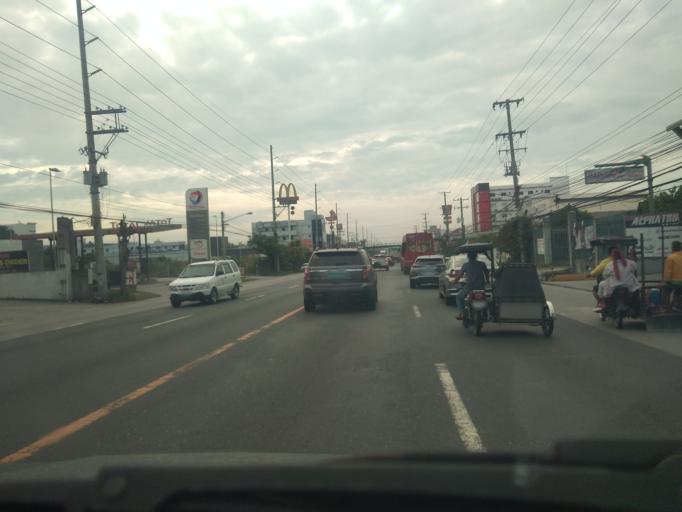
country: PH
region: Central Luzon
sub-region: Province of Pampanga
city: Bulaon
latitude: 15.0660
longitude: 120.6509
